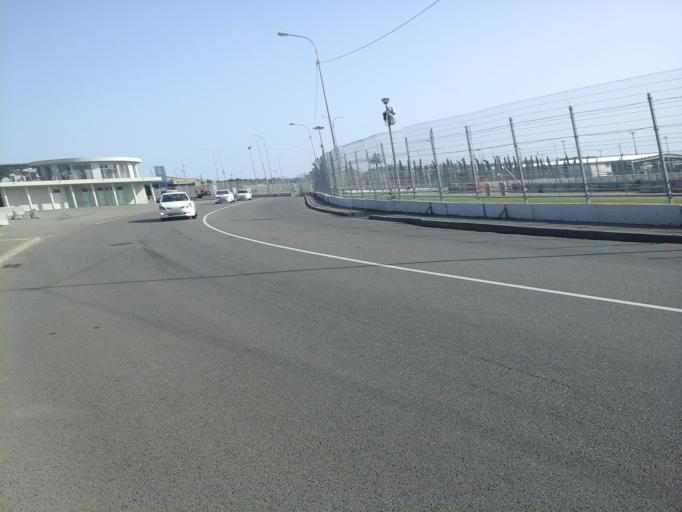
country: RU
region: Krasnodarskiy
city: Adler
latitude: 43.4128
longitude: 39.9703
